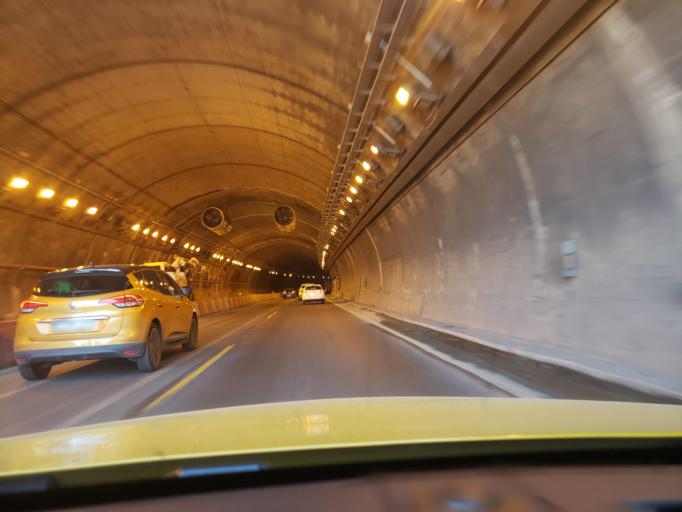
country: ES
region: Andalusia
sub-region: Provincia de Malaga
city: Marbella
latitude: 36.5143
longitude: -4.9413
